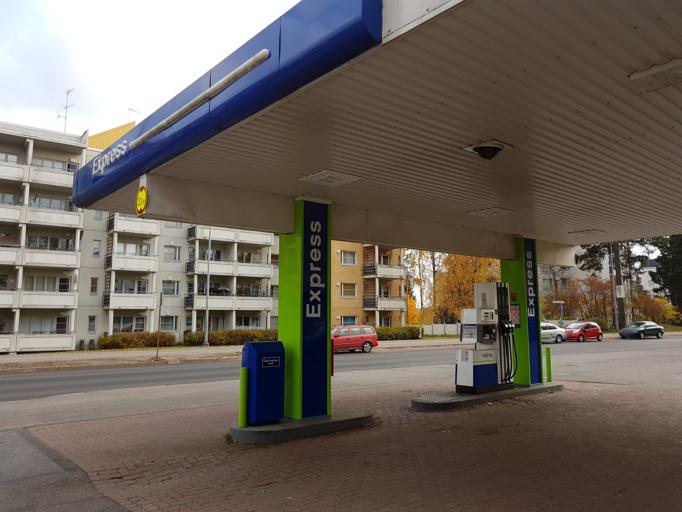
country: FI
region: Uusimaa
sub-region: Helsinki
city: Vantaa
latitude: 60.2003
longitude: 25.0590
